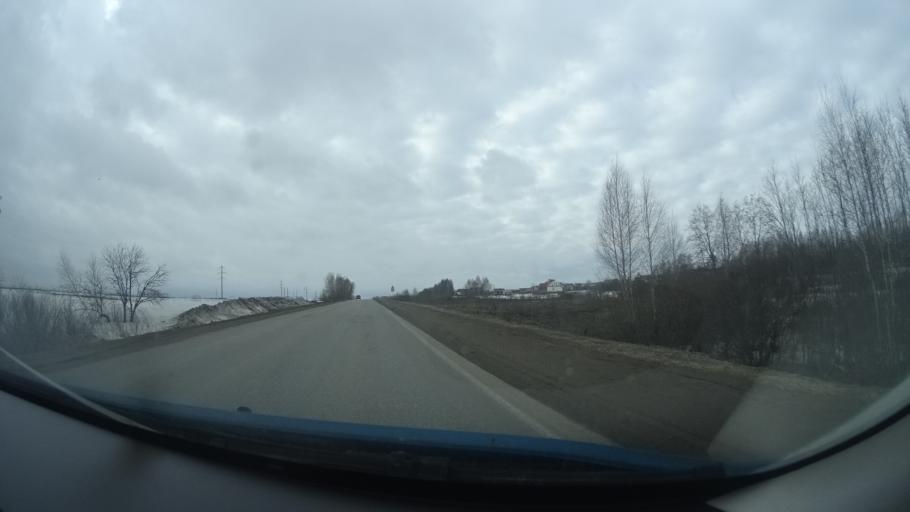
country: RU
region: Bashkortostan
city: Birsk
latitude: 55.4518
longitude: 55.5907
